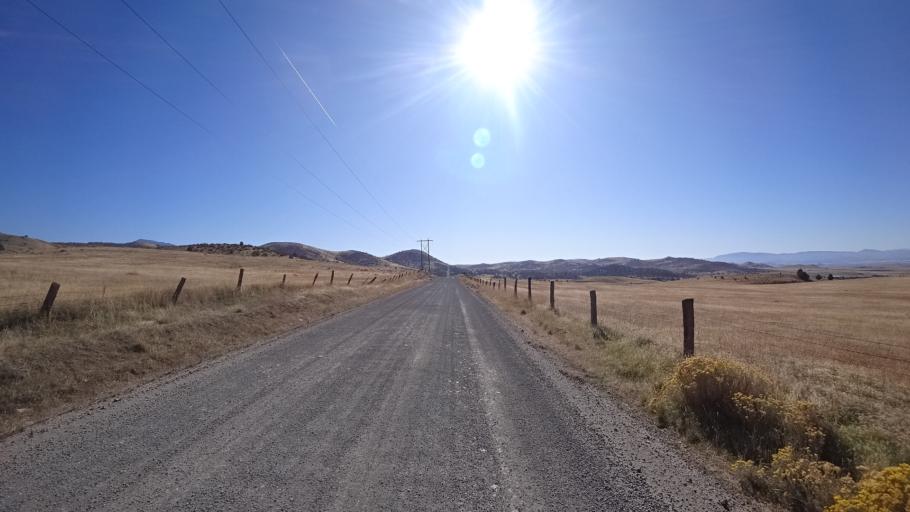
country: US
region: California
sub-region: Siskiyou County
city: Montague
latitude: 41.8257
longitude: -122.3623
